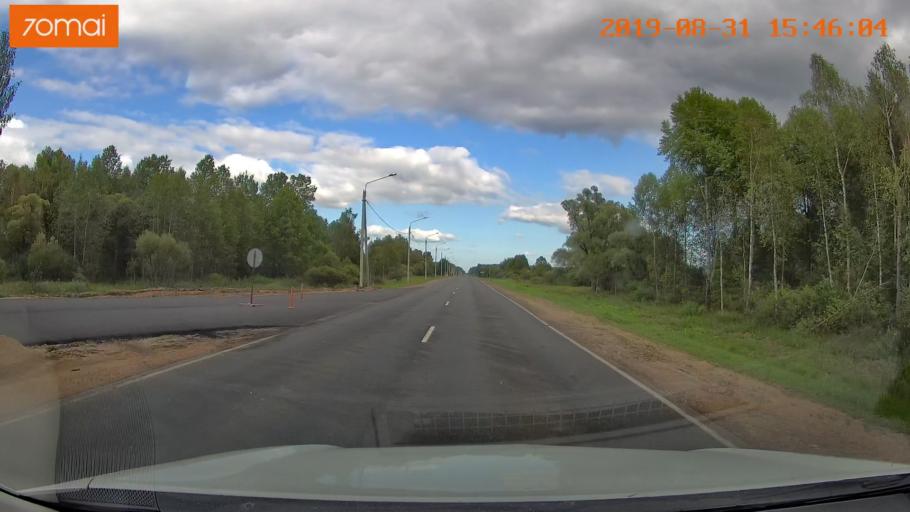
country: RU
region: Kaluga
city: Mosal'sk
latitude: 54.6705
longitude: 34.9747
